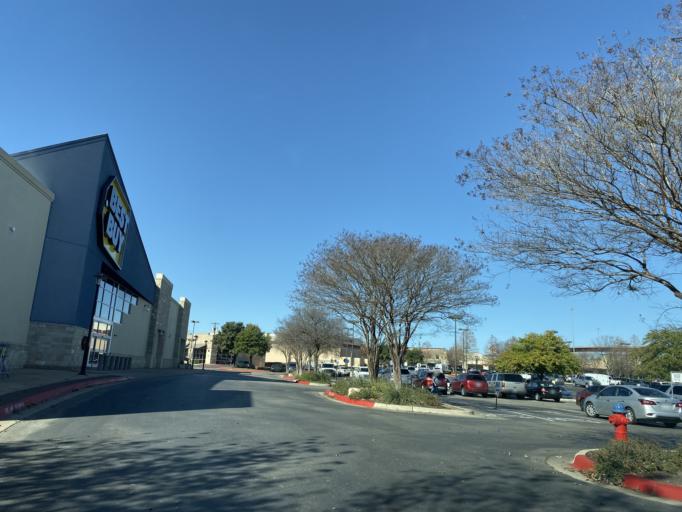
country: US
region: Texas
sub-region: Travis County
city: Windemere
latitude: 30.4761
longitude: -97.6705
